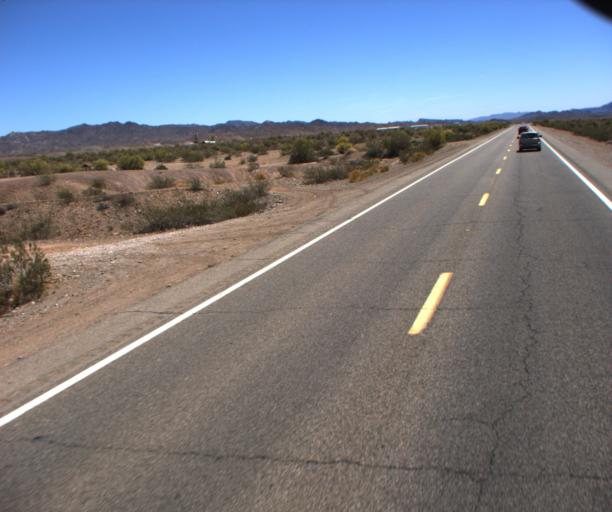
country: US
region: Arizona
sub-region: Mohave County
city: Lake Havasu City
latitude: 34.4199
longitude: -114.2003
